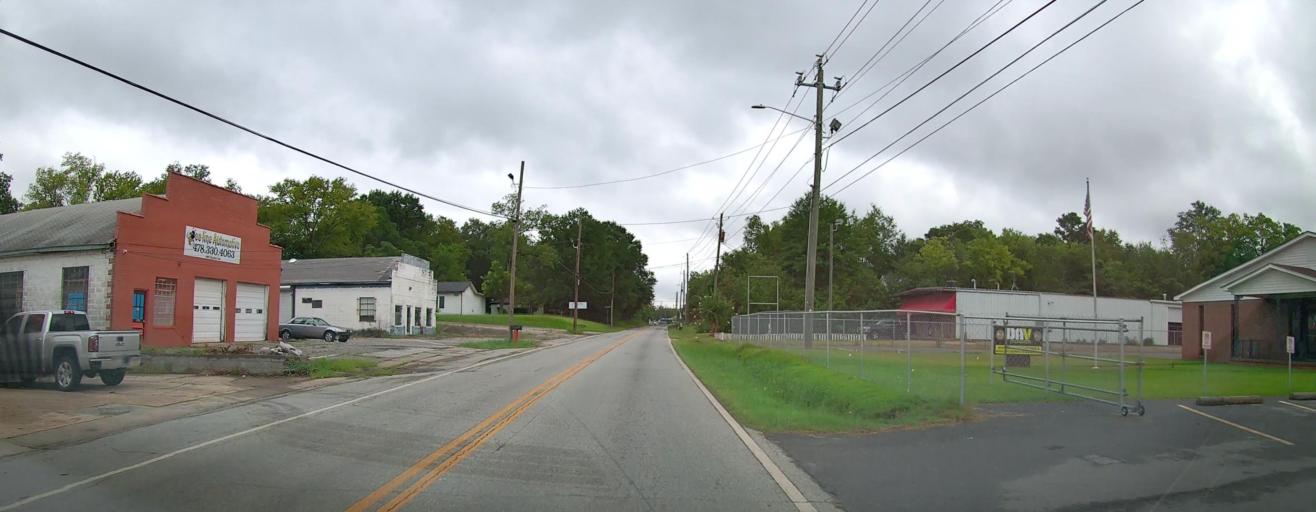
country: US
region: Georgia
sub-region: Bibb County
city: Macon
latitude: 32.7813
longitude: -83.6590
